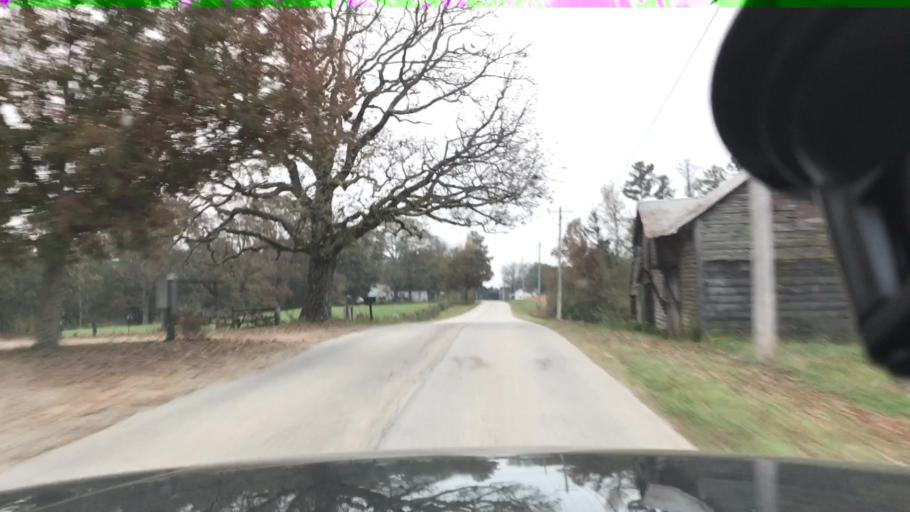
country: US
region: Georgia
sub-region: Gwinnett County
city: Buford
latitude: 34.1507
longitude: -83.9918
